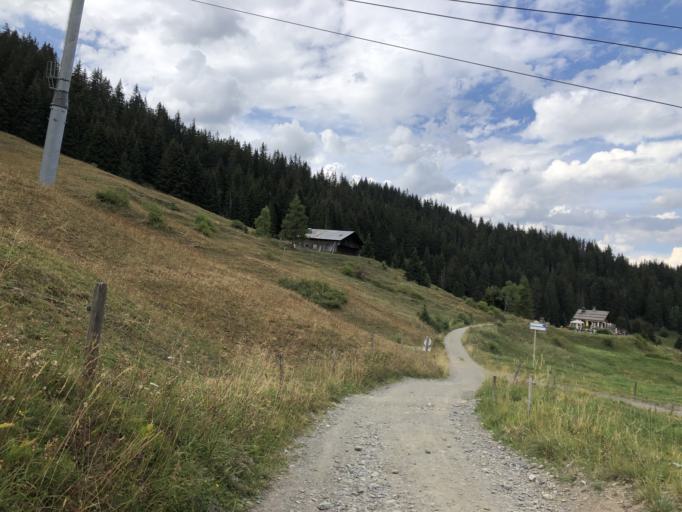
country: FR
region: Rhone-Alpes
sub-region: Departement de la Haute-Savoie
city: Megeve
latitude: 45.8739
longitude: 6.6019
